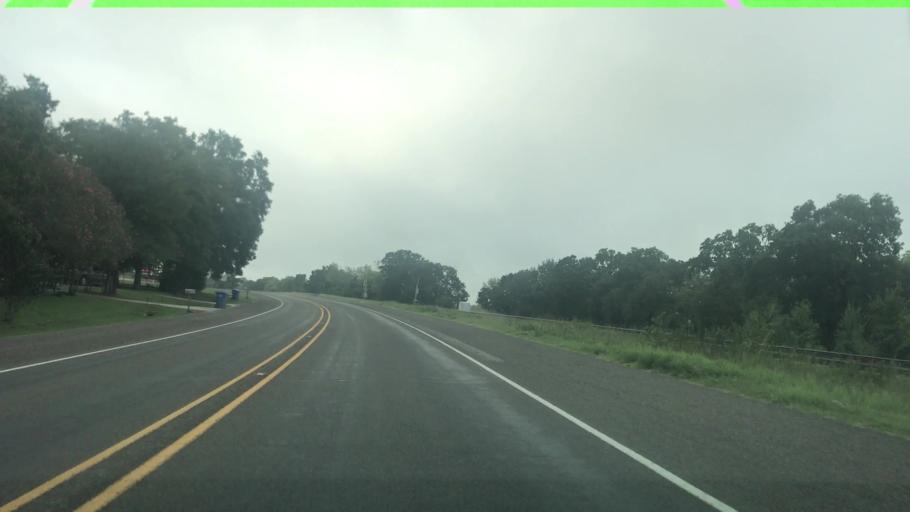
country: US
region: Texas
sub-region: Houston County
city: Cooper
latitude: 31.1219
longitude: -95.4449
